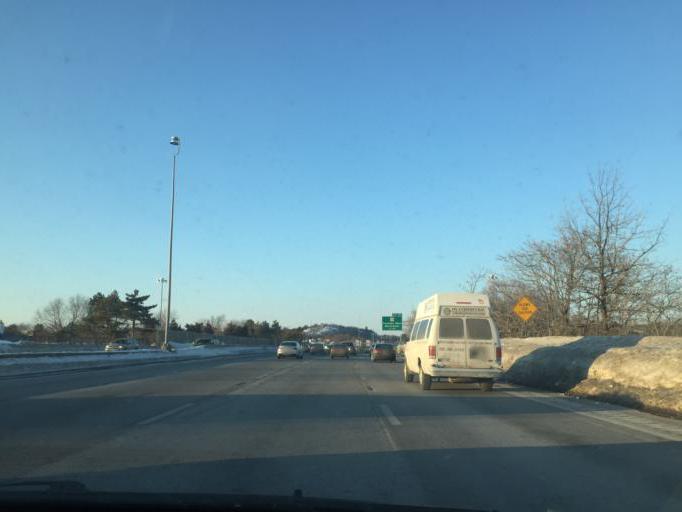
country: US
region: Massachusetts
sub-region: Middlesex County
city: Medford
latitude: 42.4180
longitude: -71.1039
